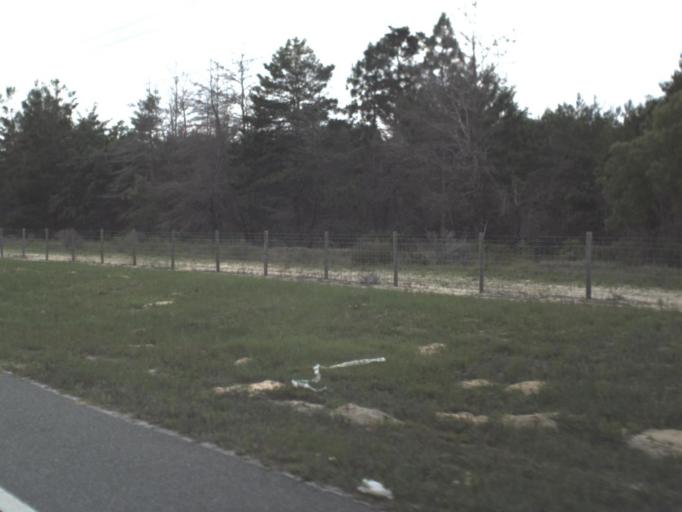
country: US
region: Florida
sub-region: Clay County
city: Keystone Heights
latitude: 29.8521
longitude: -81.9571
